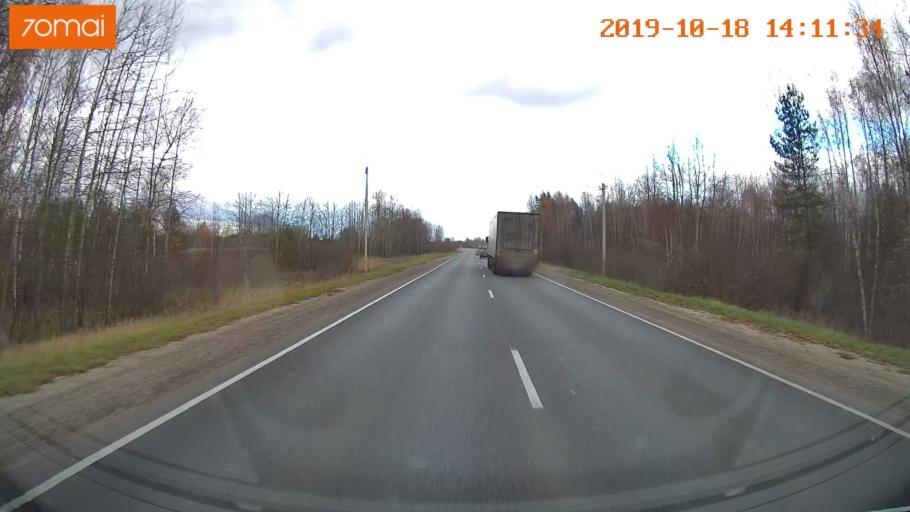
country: RU
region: Rjazan
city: Spas-Klepiki
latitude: 55.1399
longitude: 40.2285
